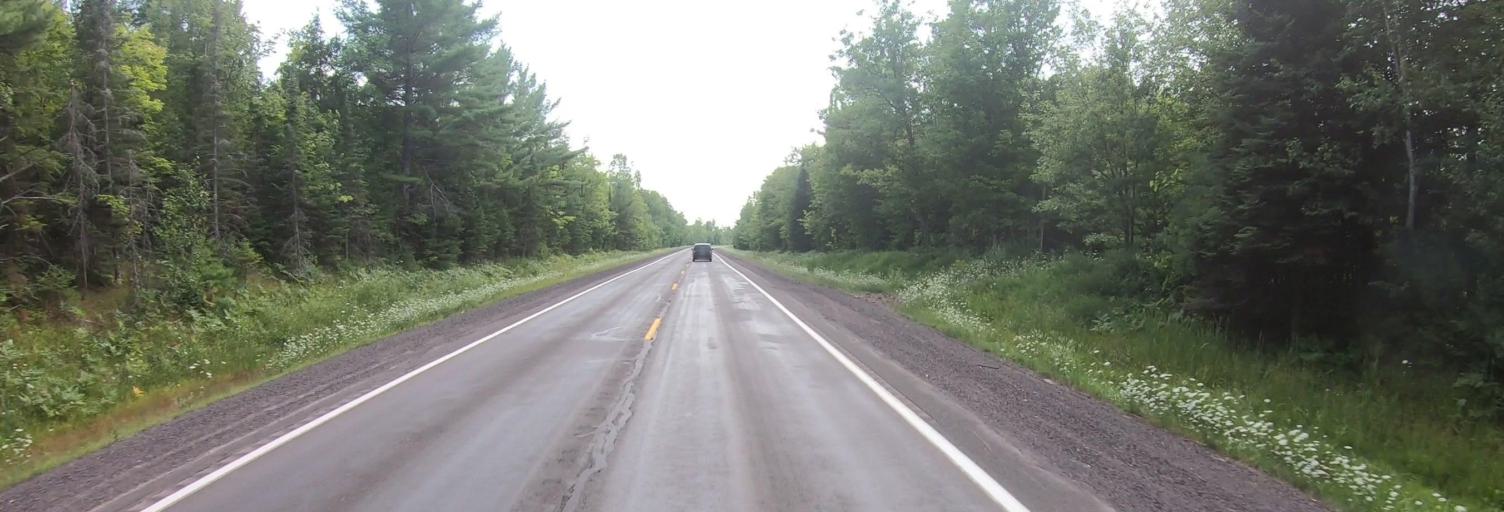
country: US
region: Michigan
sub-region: Ontonagon County
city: Ontonagon
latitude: 46.7397
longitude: -89.1095
